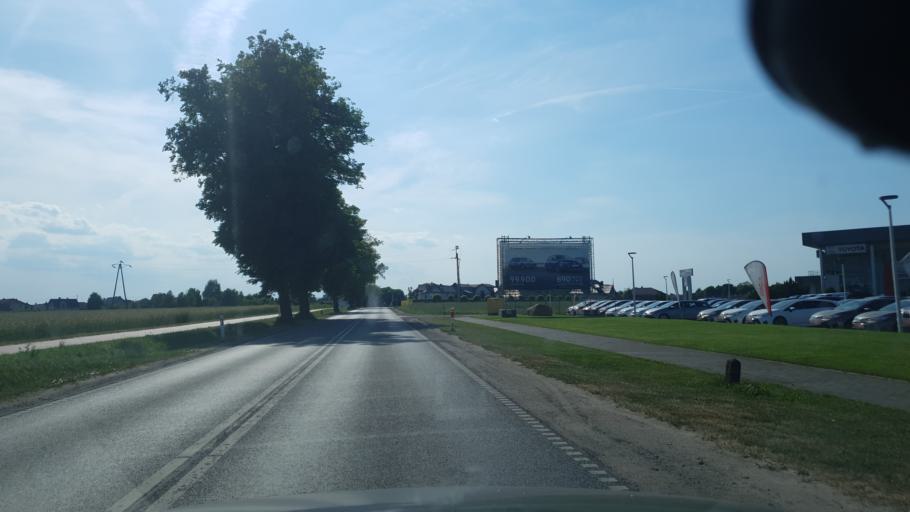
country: PL
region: Pomeranian Voivodeship
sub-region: Powiat kartuski
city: Chwaszczyno
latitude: 54.4426
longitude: 18.4297
